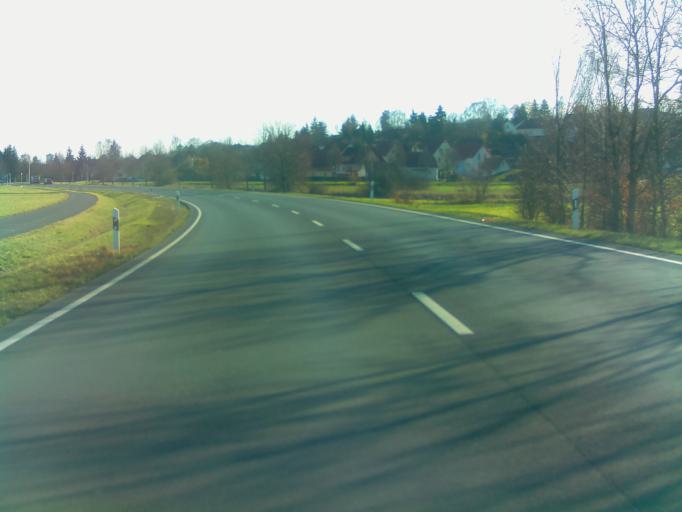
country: DE
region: Bavaria
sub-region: Regierungsbezirk Unterfranken
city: Saal an der Saale
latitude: 50.3193
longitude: 10.3467
